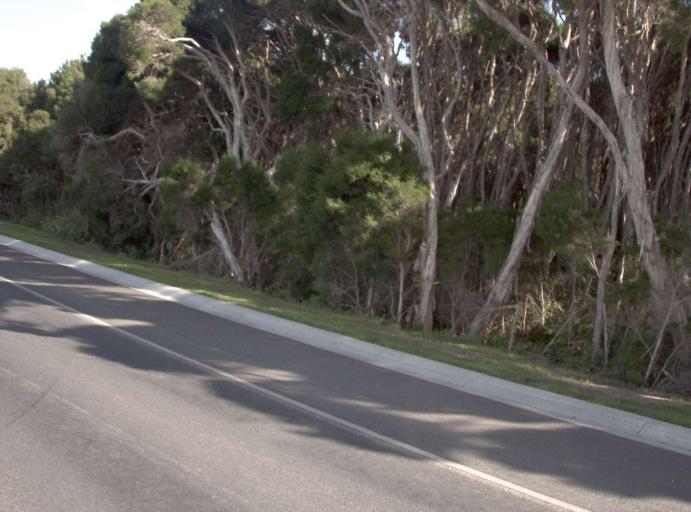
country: AU
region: Victoria
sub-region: Bass Coast
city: North Wonthaggi
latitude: -38.6055
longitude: 145.6026
